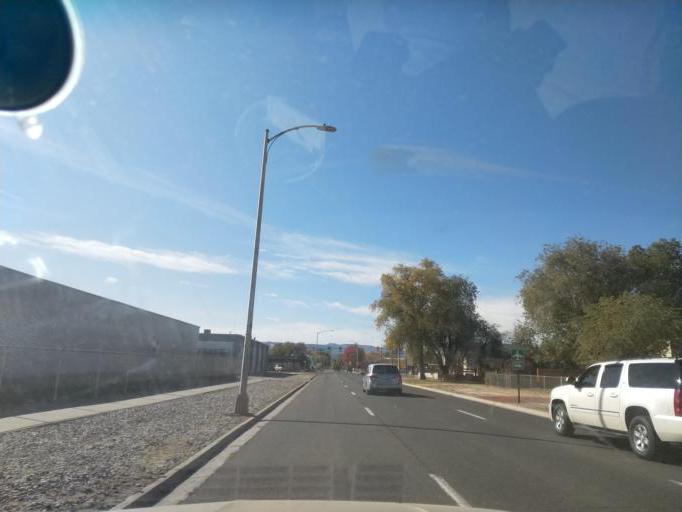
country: US
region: Colorado
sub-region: Mesa County
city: Grand Junction
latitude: 39.0653
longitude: -108.5508
